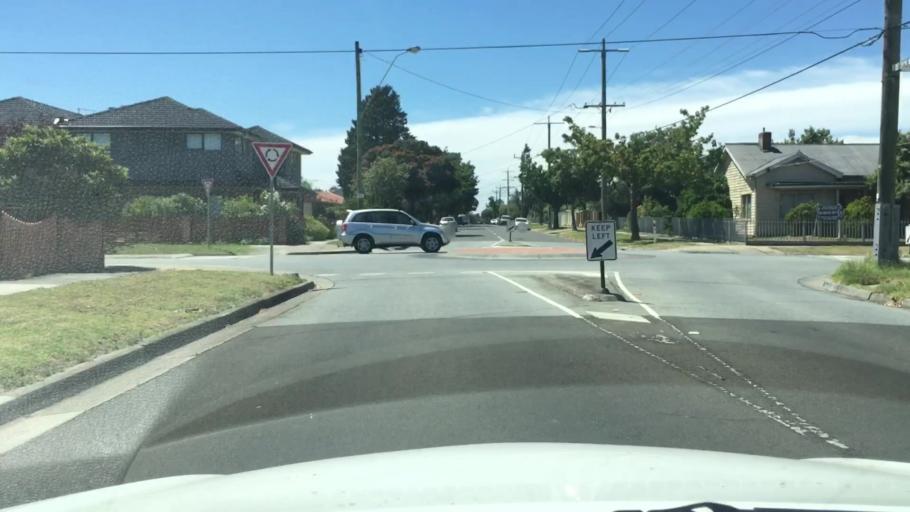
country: AU
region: Victoria
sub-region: Greater Dandenong
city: Springvale
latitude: -37.9511
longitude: 145.1435
